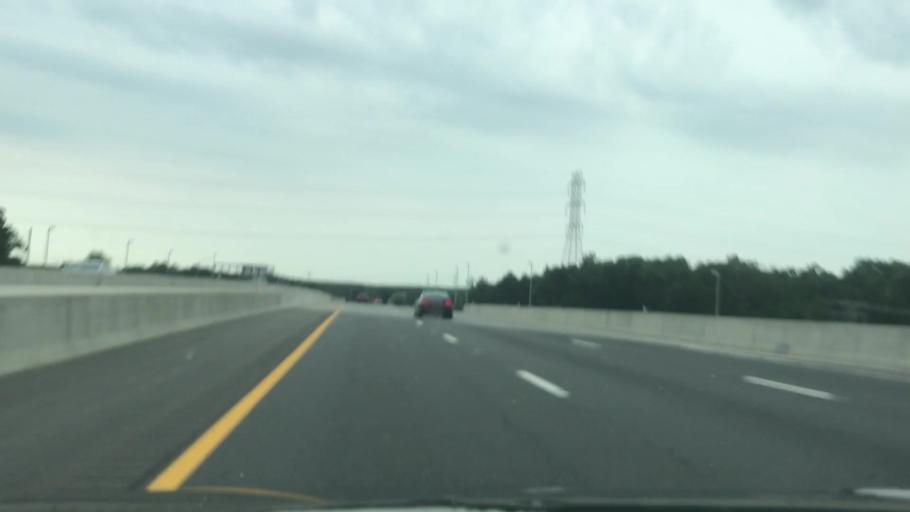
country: US
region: New Jersey
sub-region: Ocean County
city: Silver Ridge
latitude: 39.9892
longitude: -74.2106
